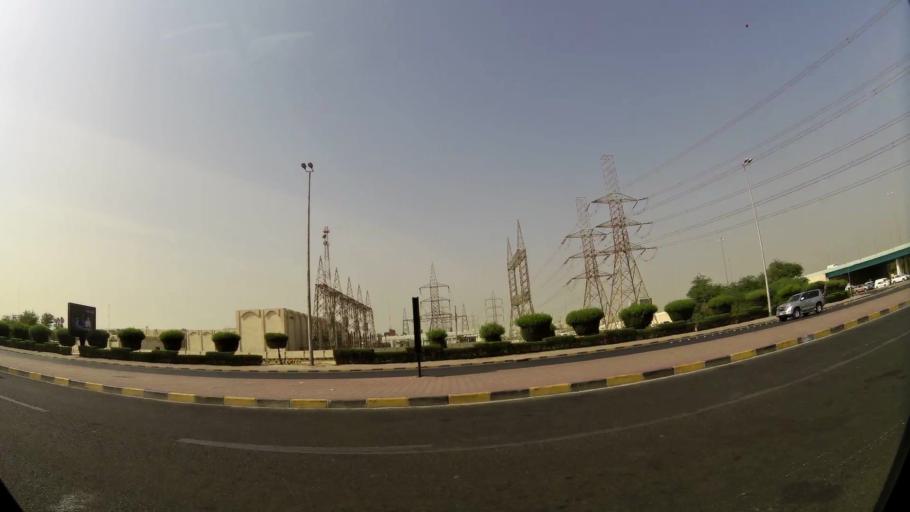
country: KW
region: Al Asimah
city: Ar Rabiyah
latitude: 29.2995
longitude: 47.9278
